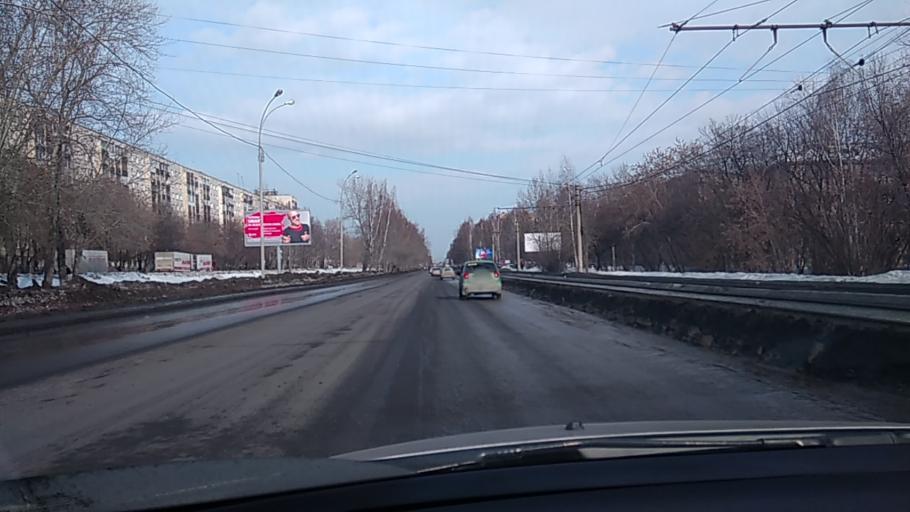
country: RU
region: Sverdlovsk
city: Yekaterinburg
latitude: 56.8538
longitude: 60.6464
